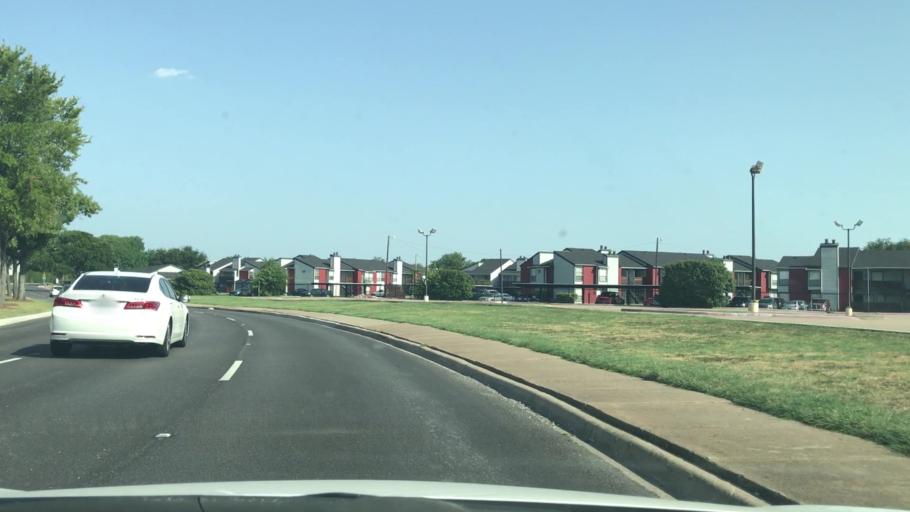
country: US
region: Texas
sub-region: Collin County
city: Plano
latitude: 33.0254
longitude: -96.7533
